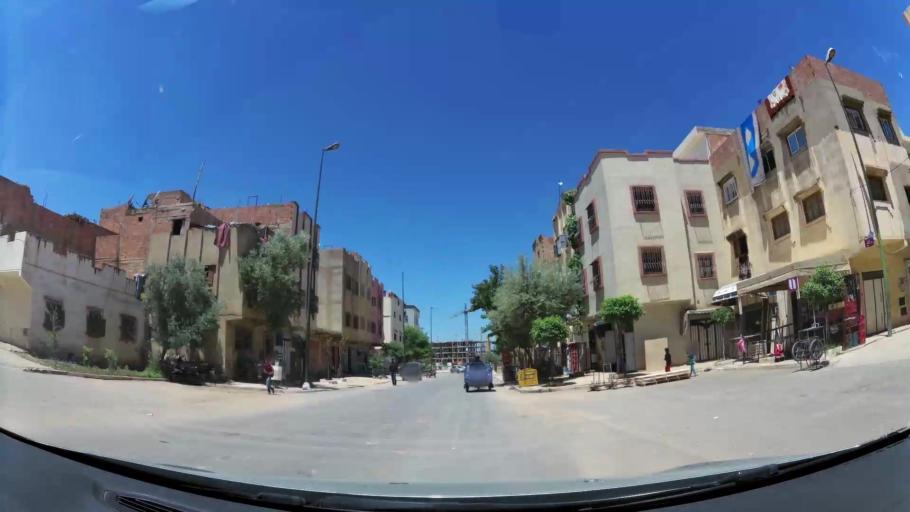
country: MA
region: Meknes-Tafilalet
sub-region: Meknes
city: Meknes
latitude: 33.8669
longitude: -5.5658
